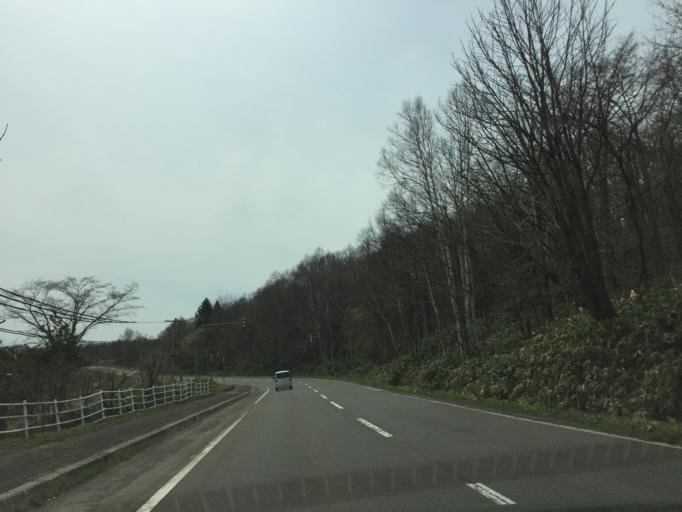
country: JP
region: Hokkaido
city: Ashibetsu
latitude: 43.5881
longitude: 142.1939
